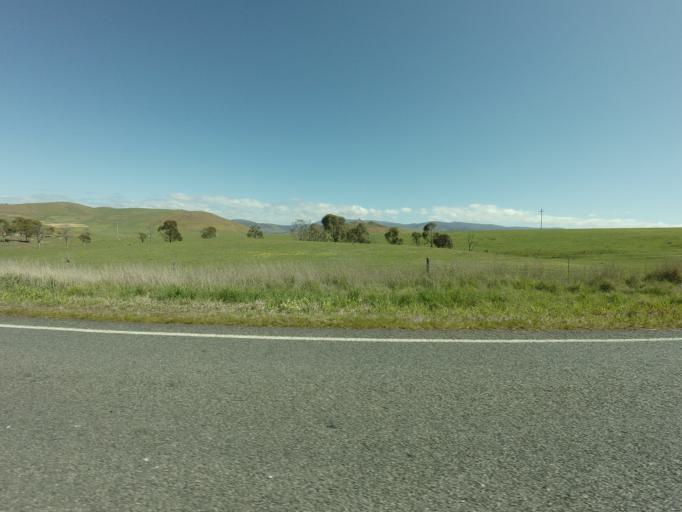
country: AU
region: Tasmania
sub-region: Derwent Valley
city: New Norfolk
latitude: -42.5412
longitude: 146.7725
